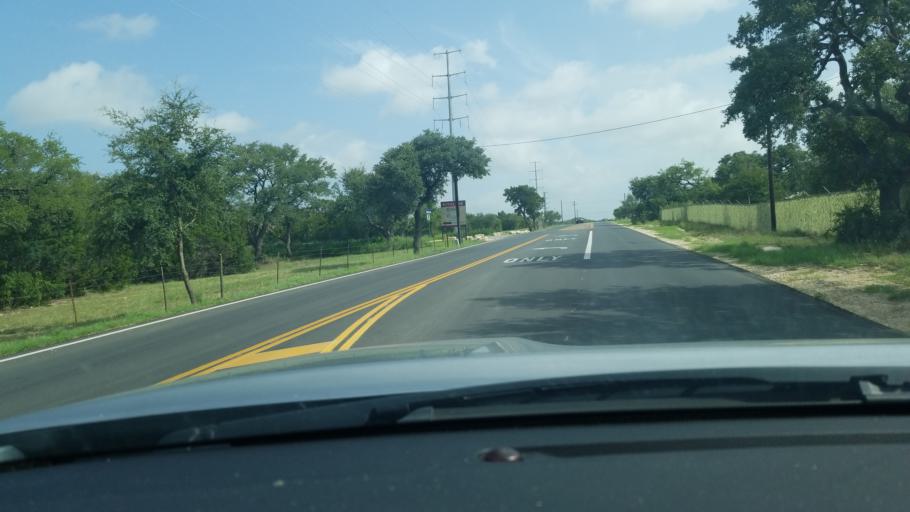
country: US
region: Texas
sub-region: Bexar County
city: Timberwood Park
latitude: 29.6962
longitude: -98.4543
